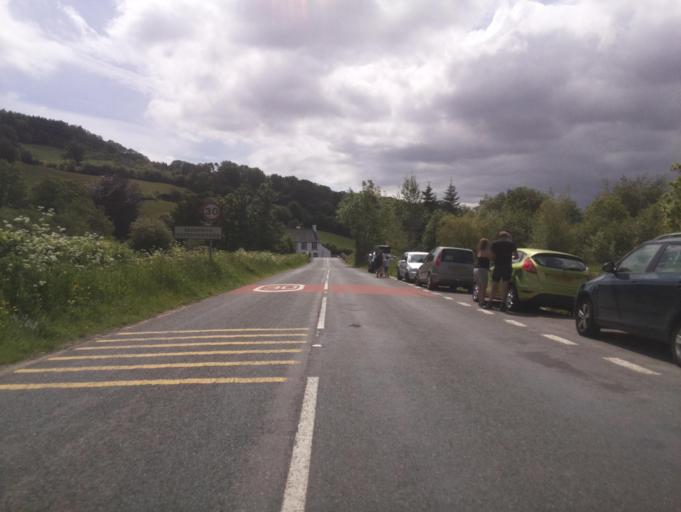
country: GB
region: England
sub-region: Herefordshire
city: Llanrothal
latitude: 51.8786
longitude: -2.7877
